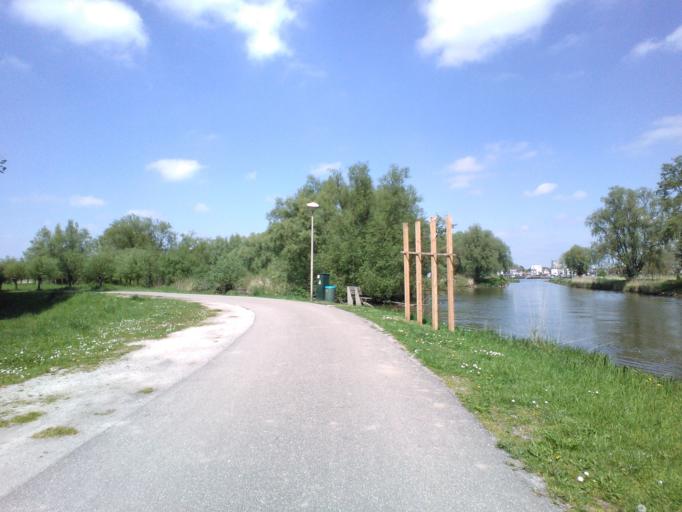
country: NL
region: South Holland
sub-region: Gemeente Sliedrecht
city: Sliedrecht
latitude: 51.8111
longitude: 4.7817
